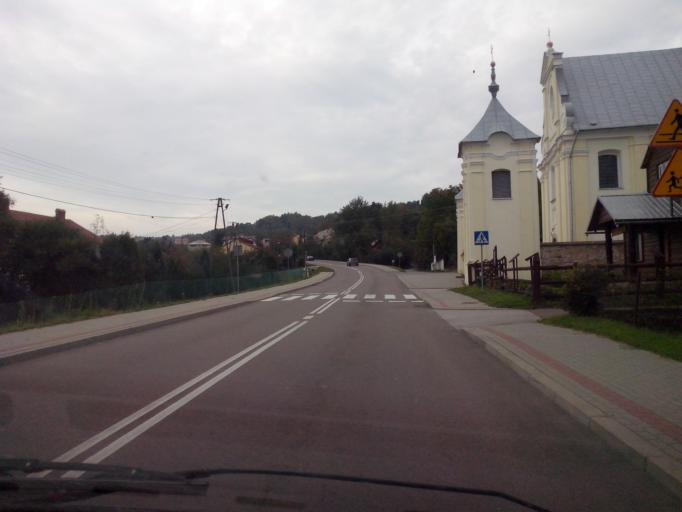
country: PL
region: Subcarpathian Voivodeship
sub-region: Powiat jaroslawski
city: Kramarzowka
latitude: 49.8188
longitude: 22.4759
